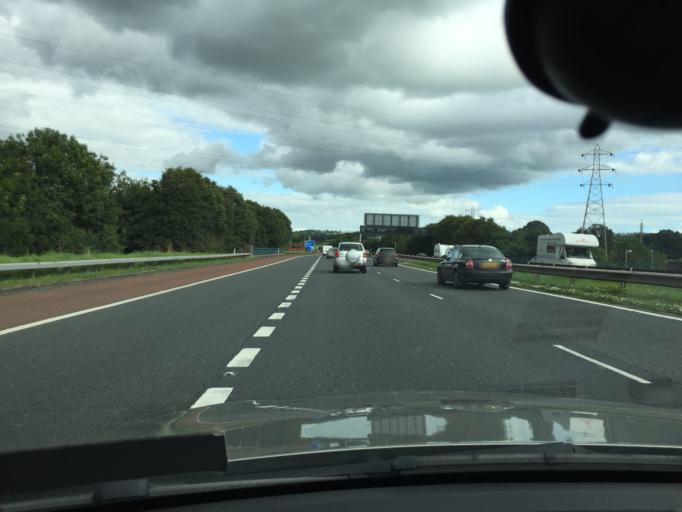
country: GB
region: Northern Ireland
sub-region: Lisburn District
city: Lisburn
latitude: 54.4944
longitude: -6.0574
